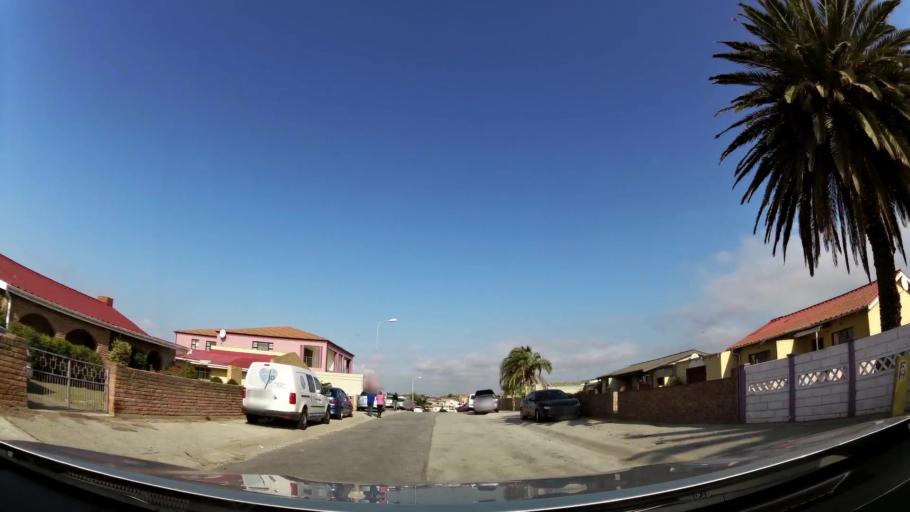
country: ZA
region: Eastern Cape
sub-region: Nelson Mandela Bay Metropolitan Municipality
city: Port Elizabeth
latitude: -33.9232
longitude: 25.5387
